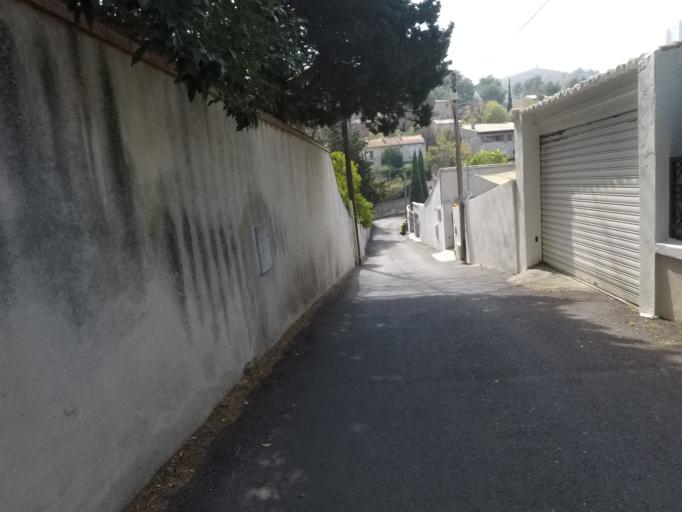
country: FR
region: Provence-Alpes-Cote d'Azur
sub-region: Departement des Bouches-du-Rhone
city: Marseille 09
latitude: 43.2559
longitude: 5.4316
